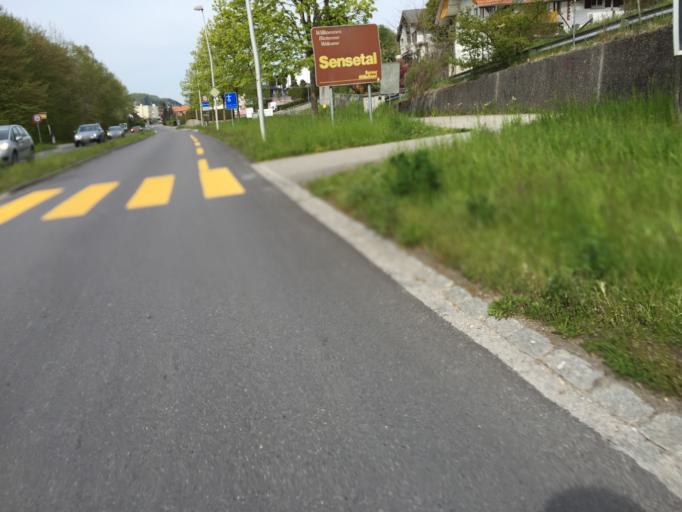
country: CH
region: Fribourg
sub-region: Sense District
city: Flamatt
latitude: 46.8942
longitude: 7.3239
